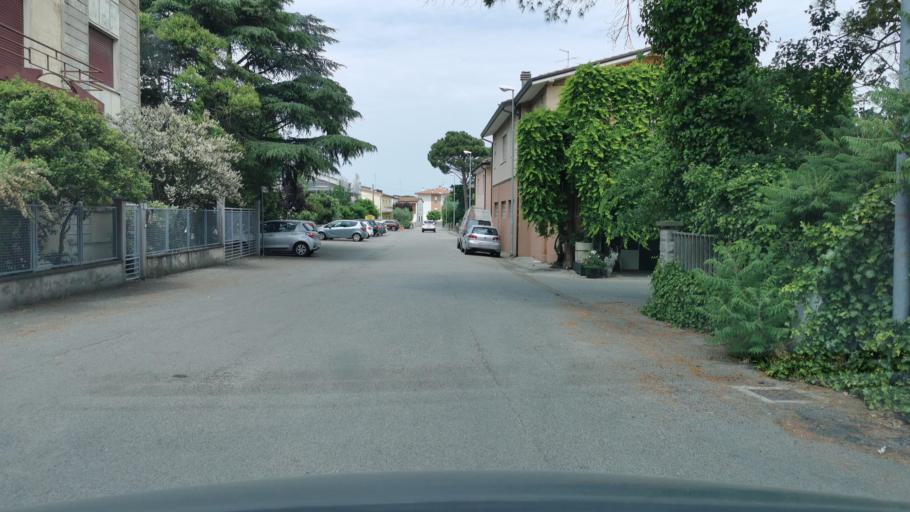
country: IT
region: Emilia-Romagna
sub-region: Provincia di Ravenna
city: Bagnacavallo
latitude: 44.4133
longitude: 11.9696
